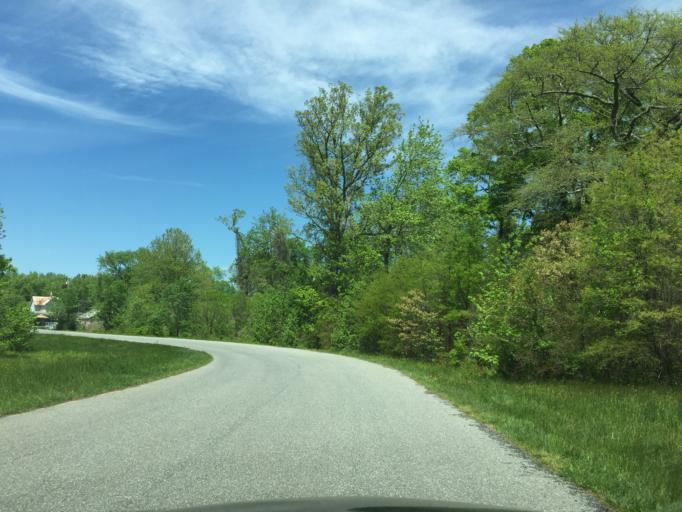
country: US
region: Maryland
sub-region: Baltimore County
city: Bowleys Quarters
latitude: 39.3579
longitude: -76.3691
